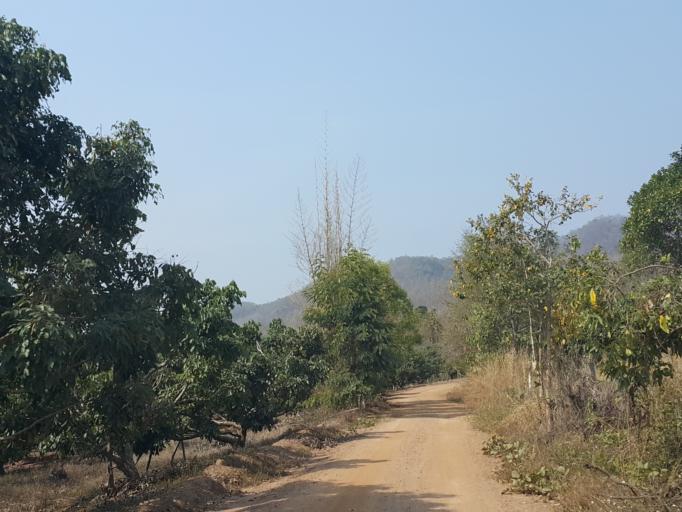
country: TH
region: Chiang Mai
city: Hang Dong
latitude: 18.7303
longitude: 98.8572
